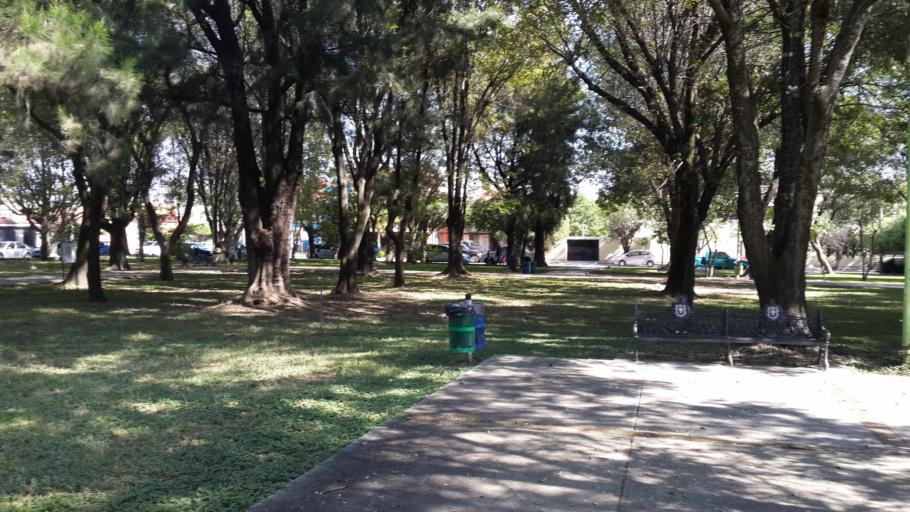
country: MX
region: Jalisco
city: Guadalajara
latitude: 20.6681
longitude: -103.4321
